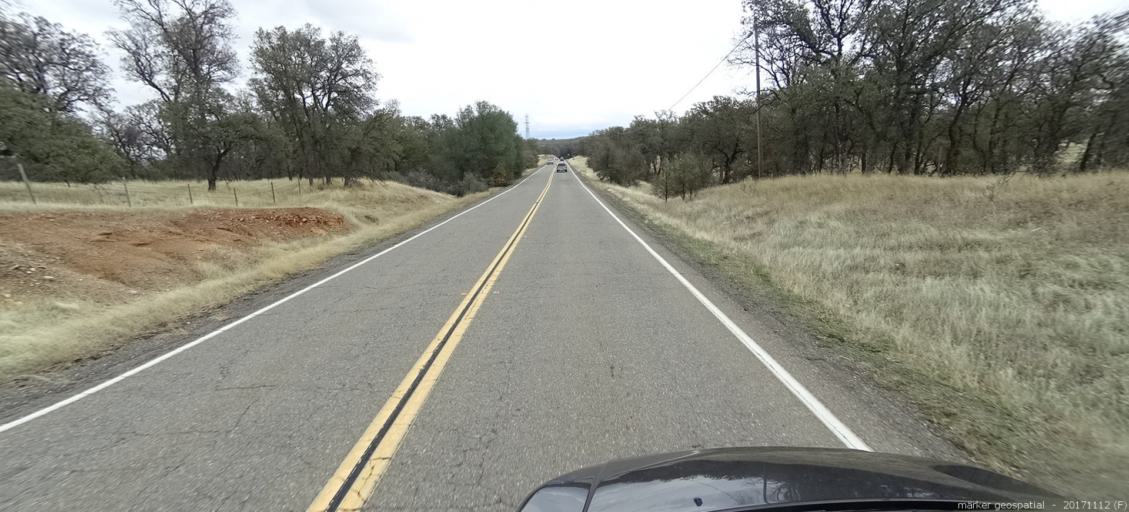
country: US
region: California
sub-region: Shasta County
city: Palo Cedro
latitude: 40.4786
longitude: -122.2114
